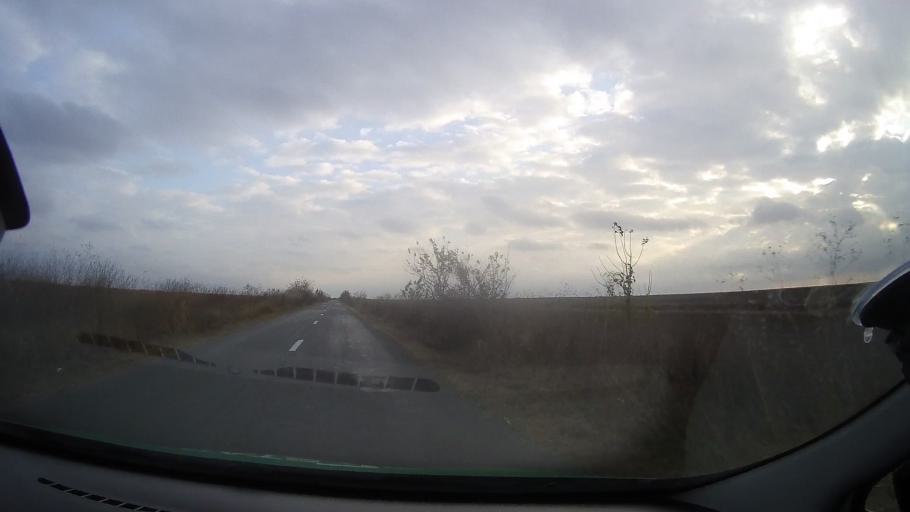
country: RO
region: Constanta
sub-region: Comuna Pestera
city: Pestera
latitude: 44.1375
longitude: 28.1181
